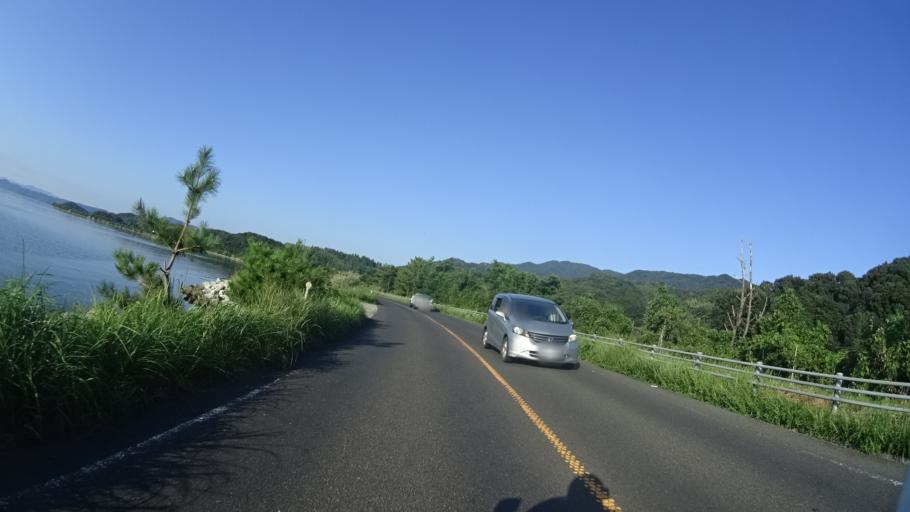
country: JP
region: Shimane
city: Sakaiminato
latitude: 35.5374
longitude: 133.1571
